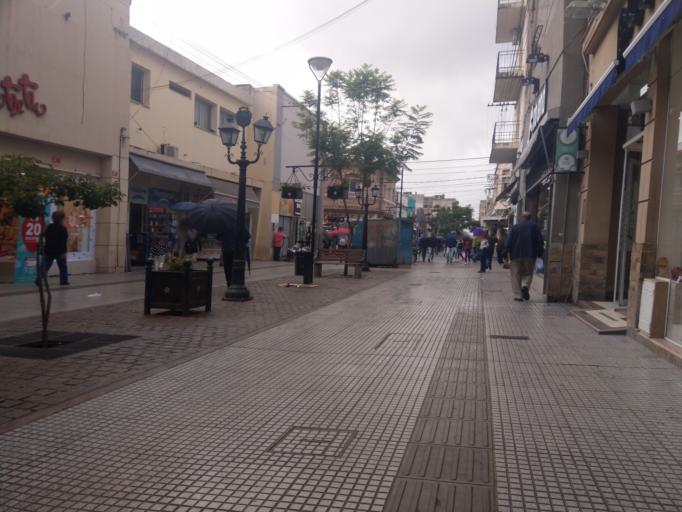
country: AR
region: Salta
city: Salta
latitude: -24.7918
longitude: -65.4126
